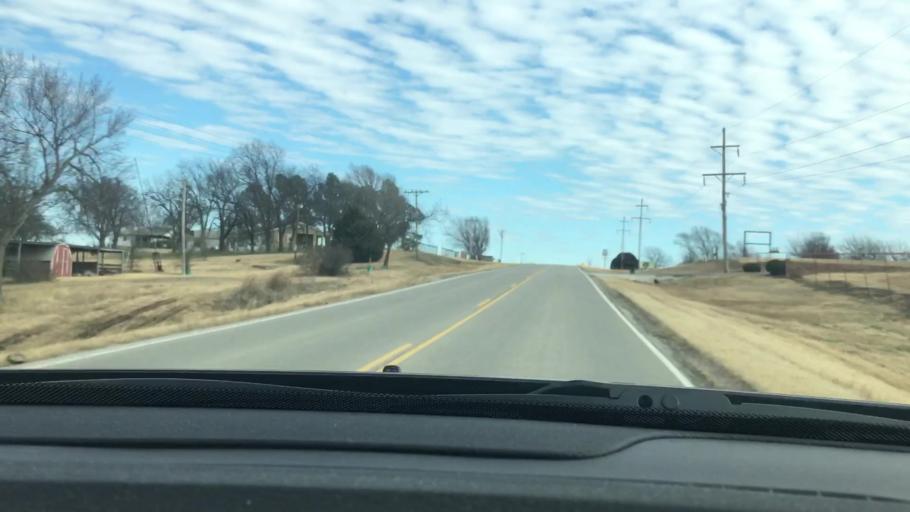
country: US
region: Oklahoma
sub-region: Garvin County
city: Pauls Valley
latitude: 34.7966
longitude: -97.1325
